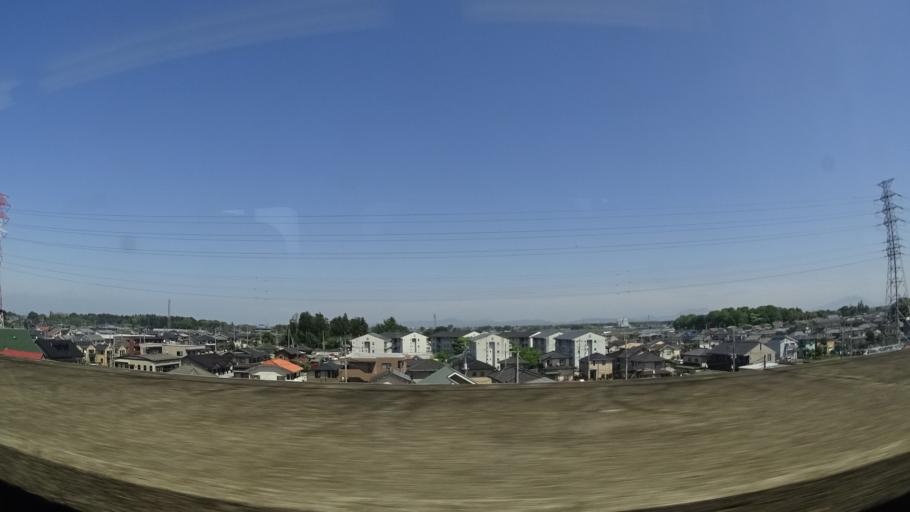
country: JP
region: Tochigi
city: Kaminokawa
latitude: 36.4363
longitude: 139.8668
